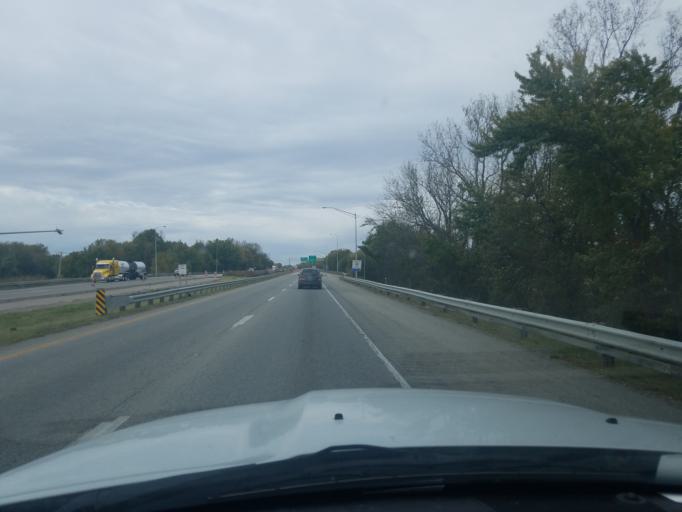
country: US
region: Indiana
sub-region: Vanderburgh County
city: Evansville
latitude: 37.9281
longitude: -87.5487
